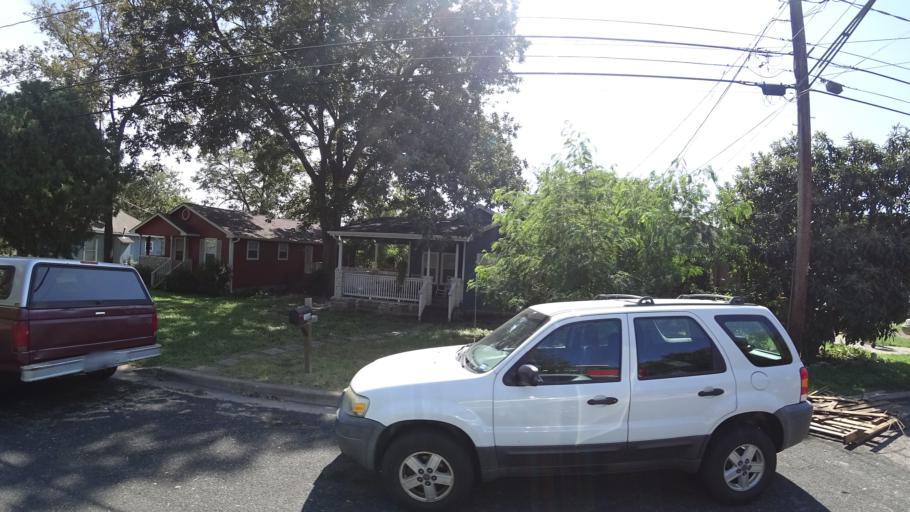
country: US
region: Texas
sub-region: Travis County
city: Austin
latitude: 30.2632
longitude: -97.7211
